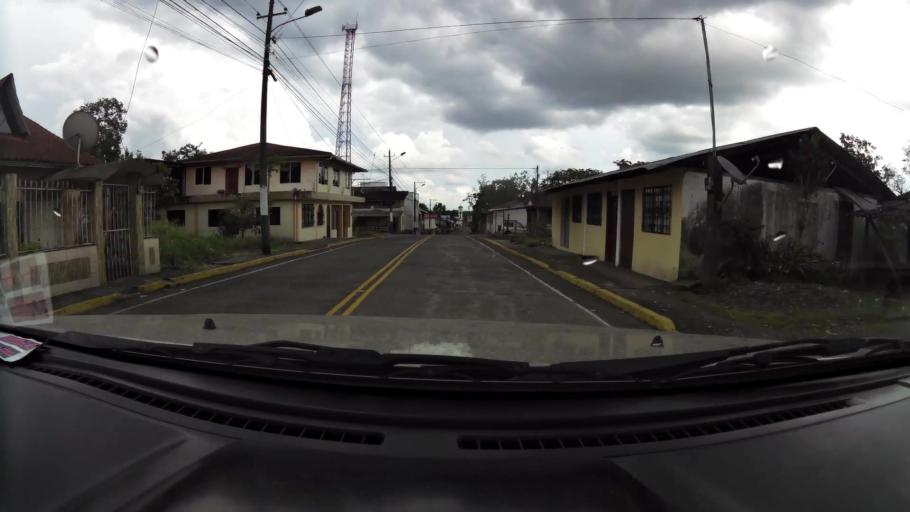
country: EC
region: Pastaza
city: Puyo
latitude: -1.4595
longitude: -78.1164
